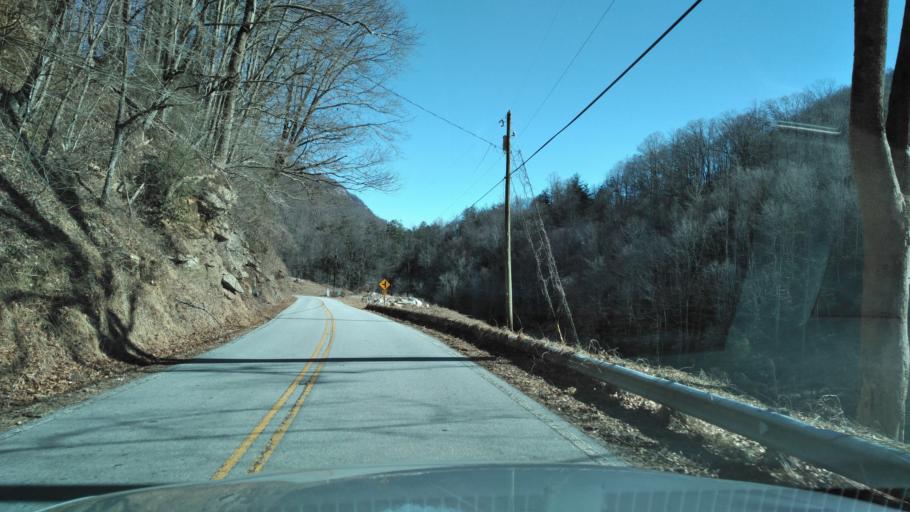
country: US
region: North Carolina
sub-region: Henderson County
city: Edneyville
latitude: 35.4608
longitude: -82.3091
